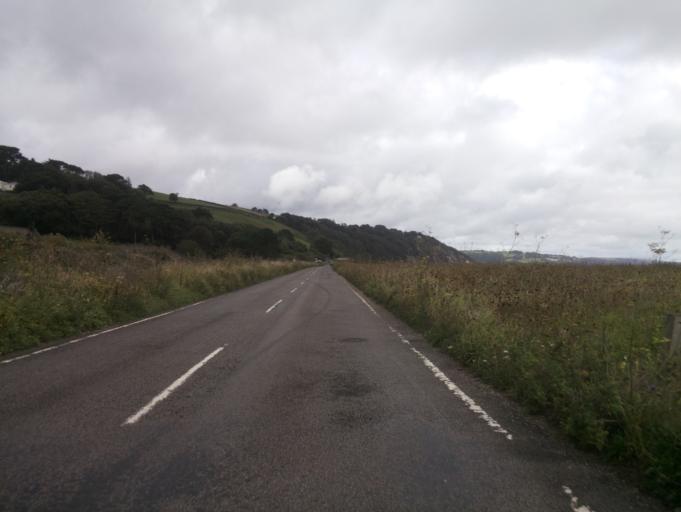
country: GB
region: England
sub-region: Devon
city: Dartmouth
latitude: 50.2960
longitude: -3.6395
